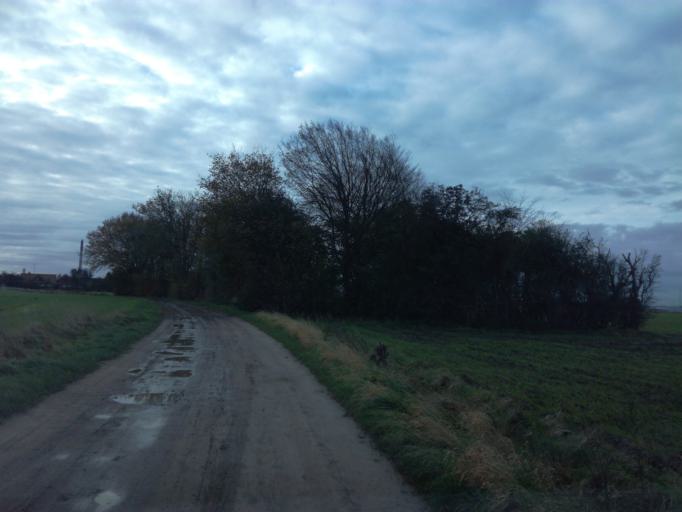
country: DK
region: South Denmark
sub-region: Fredericia Kommune
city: Fredericia
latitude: 55.6027
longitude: 9.7457
